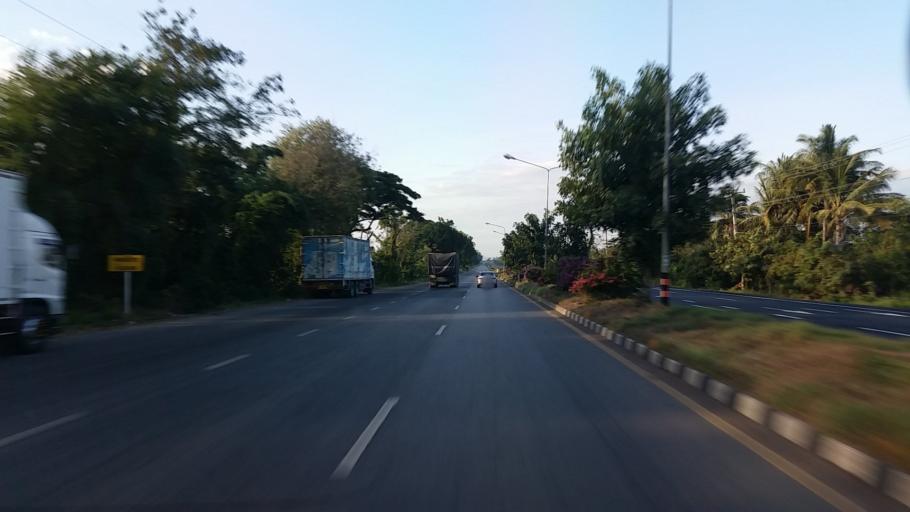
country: TH
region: Lop Buri
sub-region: Amphoe Tha Luang
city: Tha Luang
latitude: 15.1075
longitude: 101.0243
